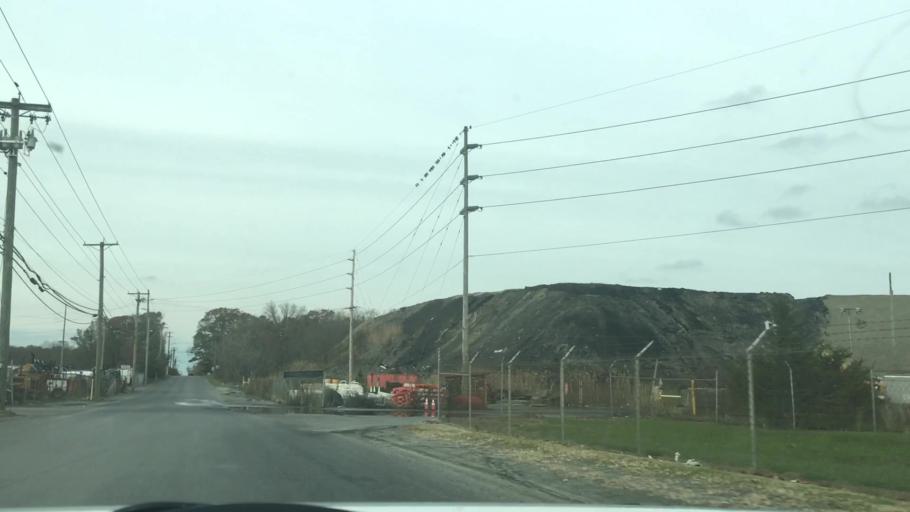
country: US
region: New Jersey
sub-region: Atlantic County
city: Pleasantville
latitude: 39.4011
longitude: -74.5374
